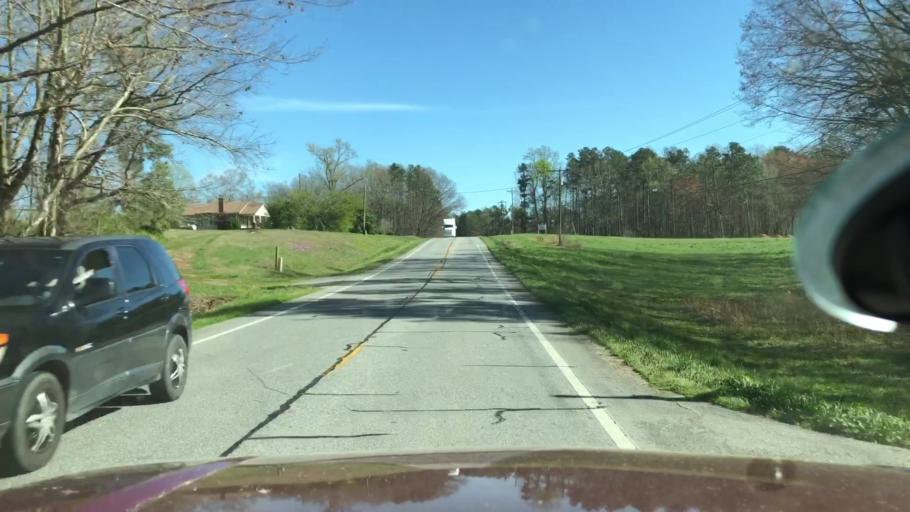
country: US
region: Georgia
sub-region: Dawson County
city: Dawsonville
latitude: 34.4504
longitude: -84.1694
